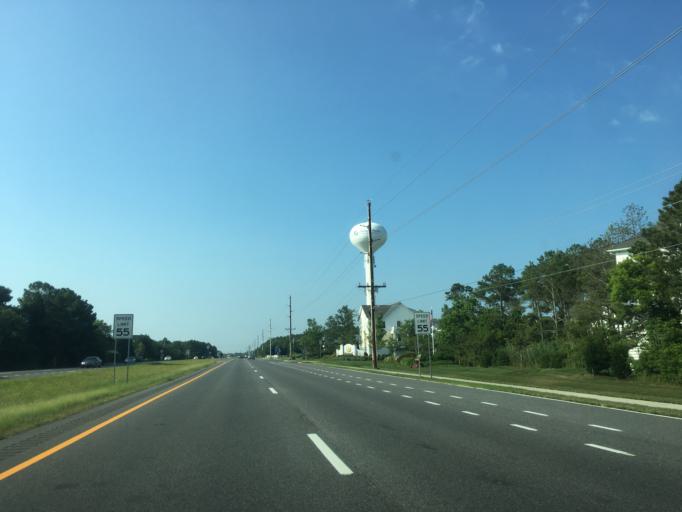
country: US
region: Delaware
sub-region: Sussex County
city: Bethany Beach
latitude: 38.5668
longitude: -75.0605
